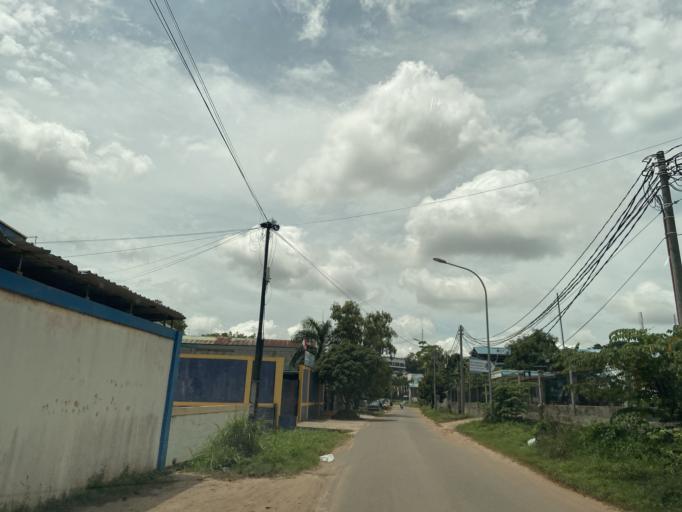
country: SG
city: Singapore
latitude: 1.1614
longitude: 104.0069
